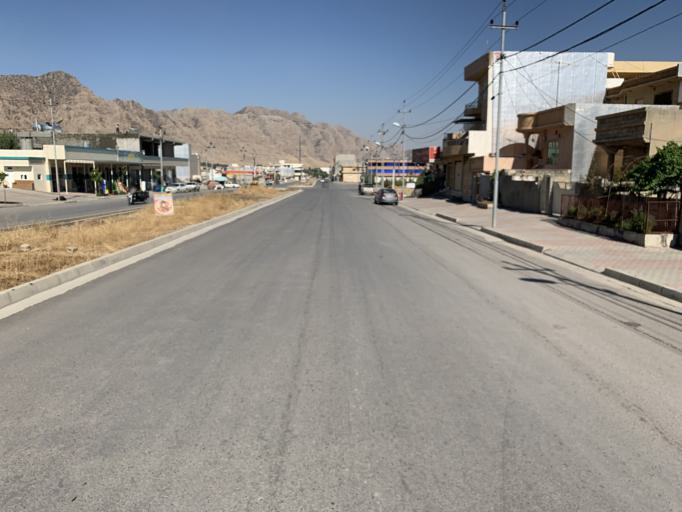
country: IQ
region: As Sulaymaniyah
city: Raniye
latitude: 36.2579
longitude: 44.8709
